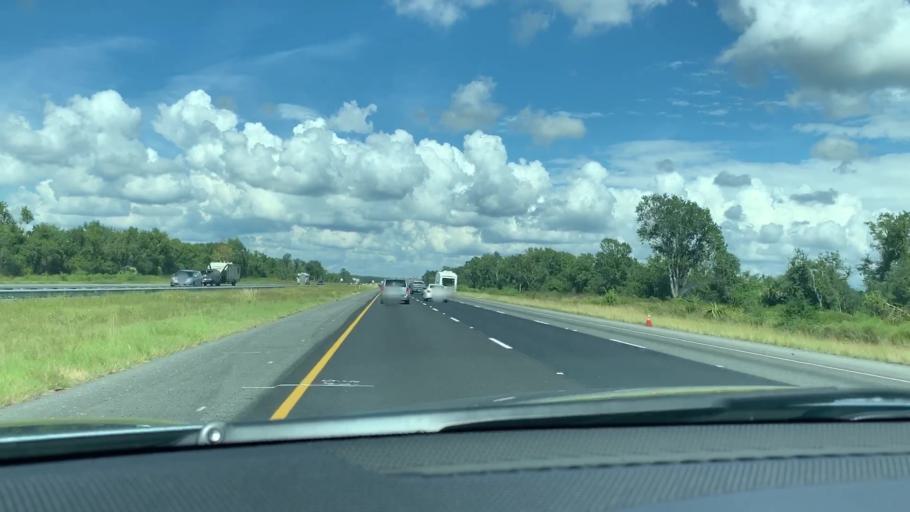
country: US
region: Georgia
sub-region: Camden County
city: Woodbine
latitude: 31.0195
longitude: -81.6580
